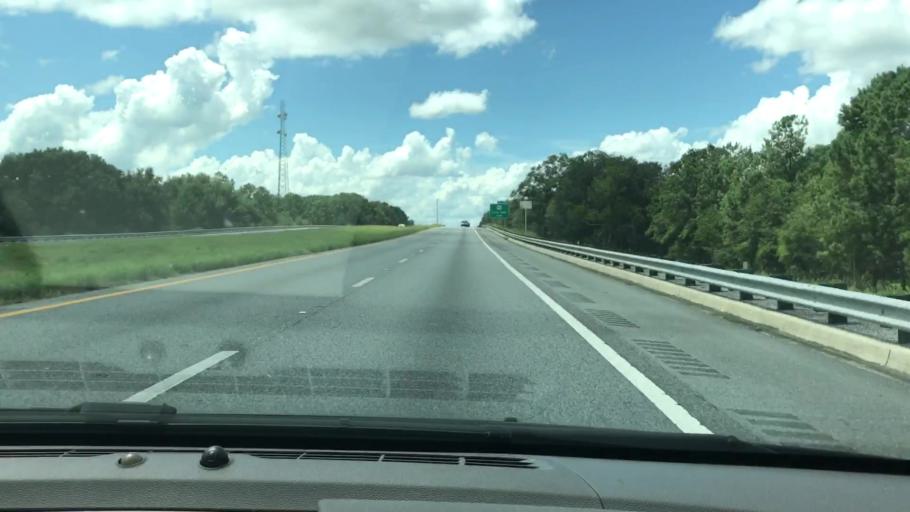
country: US
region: Florida
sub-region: Suwannee County
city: Live Oak
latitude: 30.3463
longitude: -83.0869
